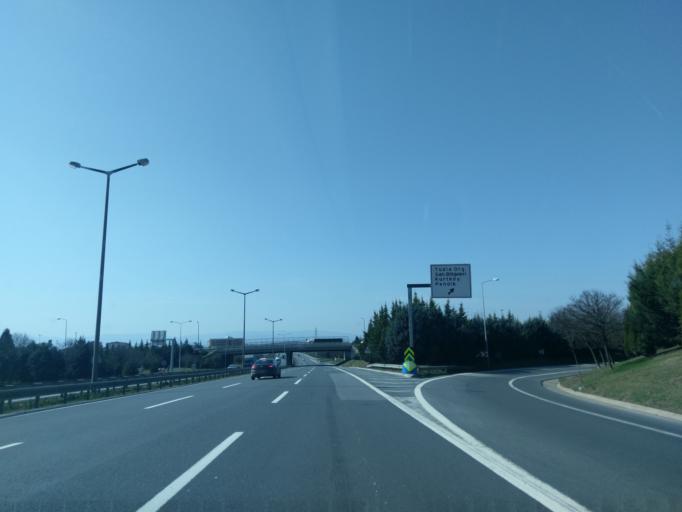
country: TR
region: Kocaeli
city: Balcik
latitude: 40.8646
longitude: 29.3851
